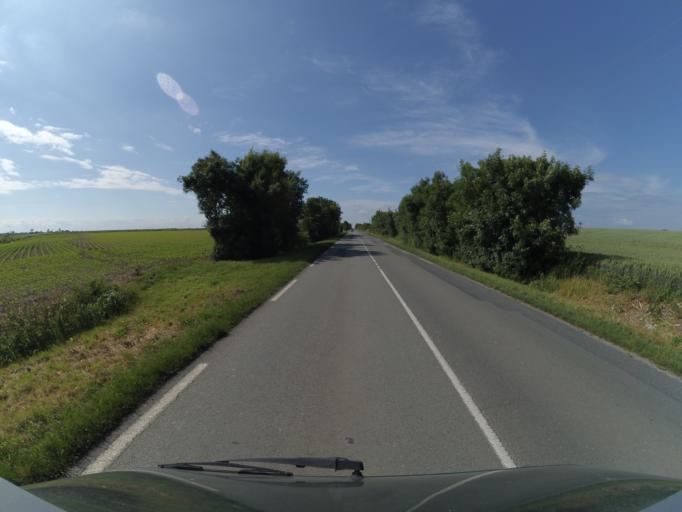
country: FR
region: Poitou-Charentes
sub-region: Departement de la Charente-Maritime
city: Andilly
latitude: 46.2492
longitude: -1.0627
